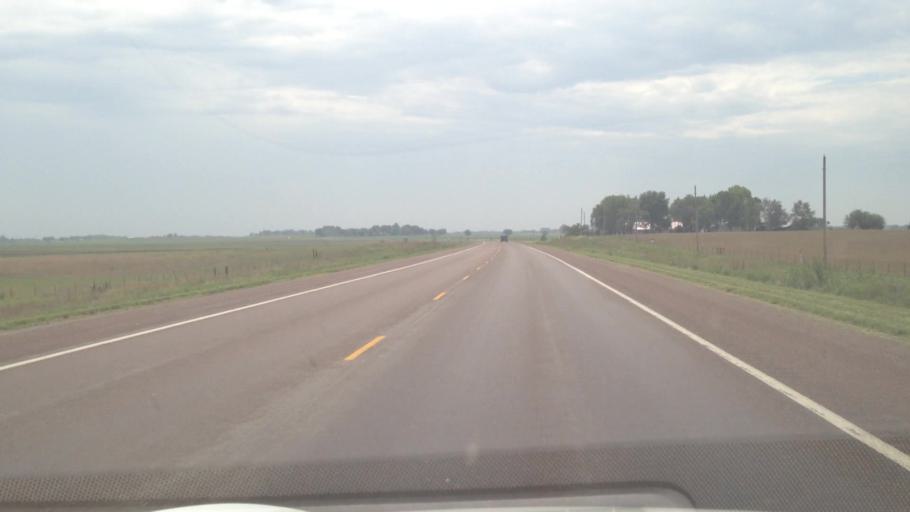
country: US
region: Kansas
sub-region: Crawford County
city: Girard
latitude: 37.4879
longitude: -94.8423
